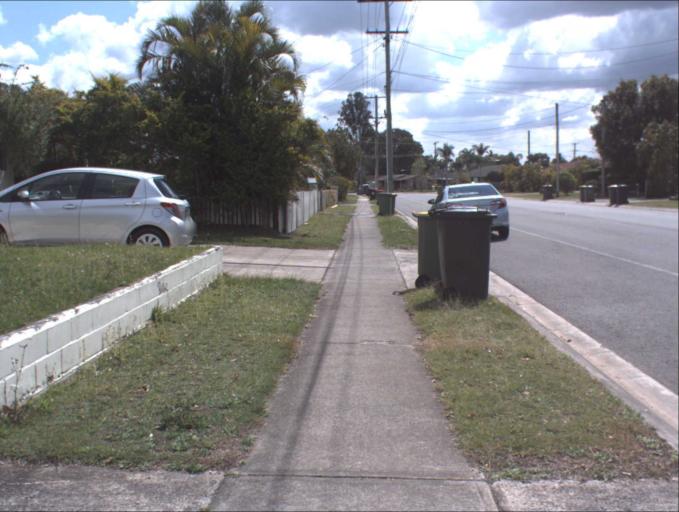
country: AU
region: Queensland
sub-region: Logan
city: Waterford West
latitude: -27.6845
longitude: 153.1533
